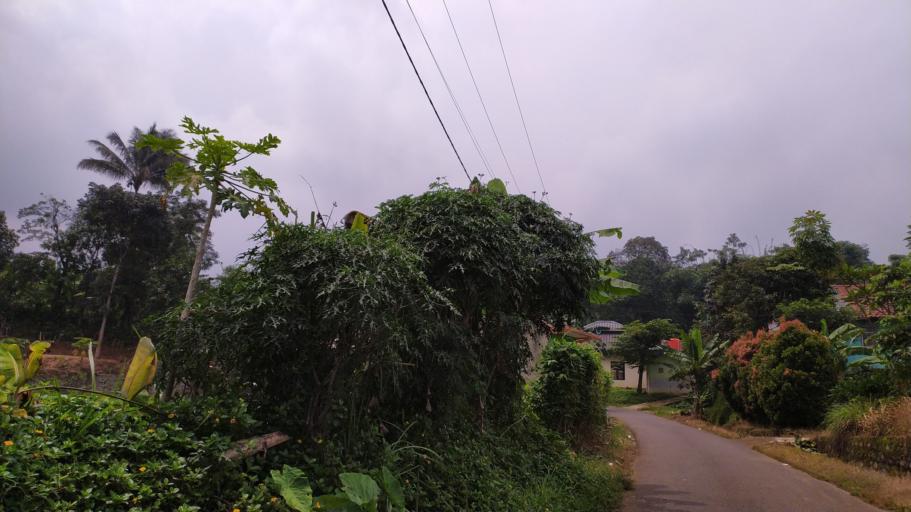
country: ID
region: West Java
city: Ciampea
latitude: -6.6217
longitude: 106.7115
